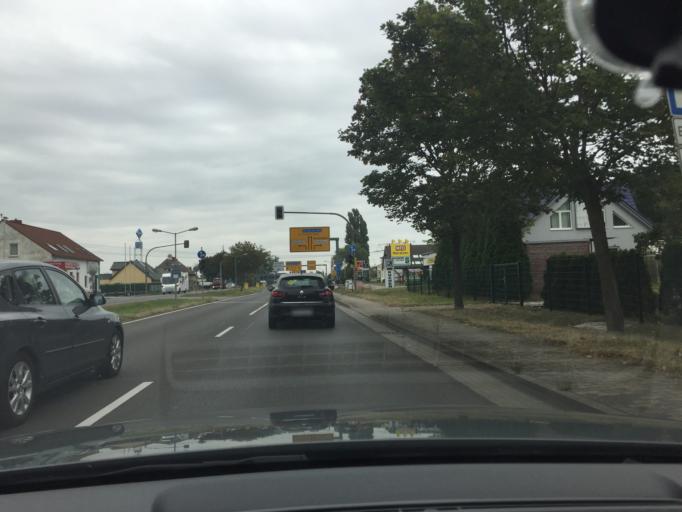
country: DE
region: Brandenburg
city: Petershagen
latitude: 52.4998
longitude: 13.7394
